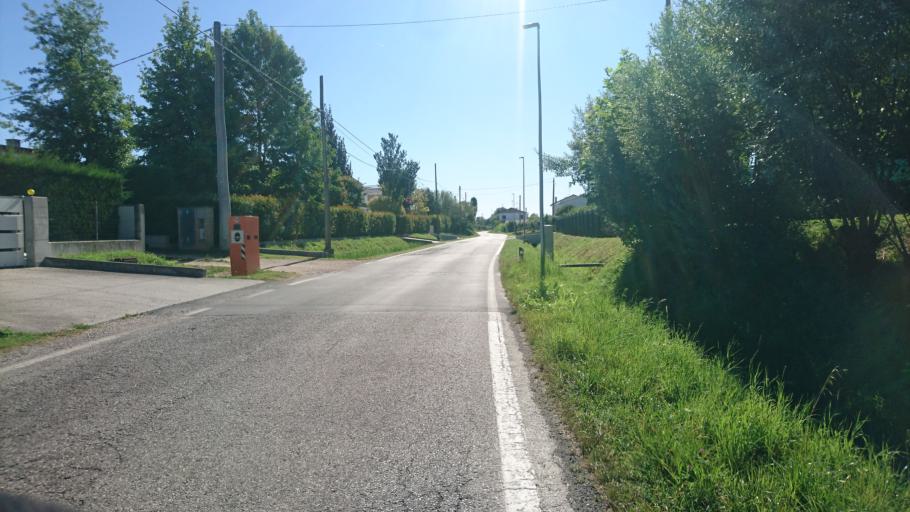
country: IT
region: Veneto
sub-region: Provincia di Padova
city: Legnaro
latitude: 45.3307
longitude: 11.9732
